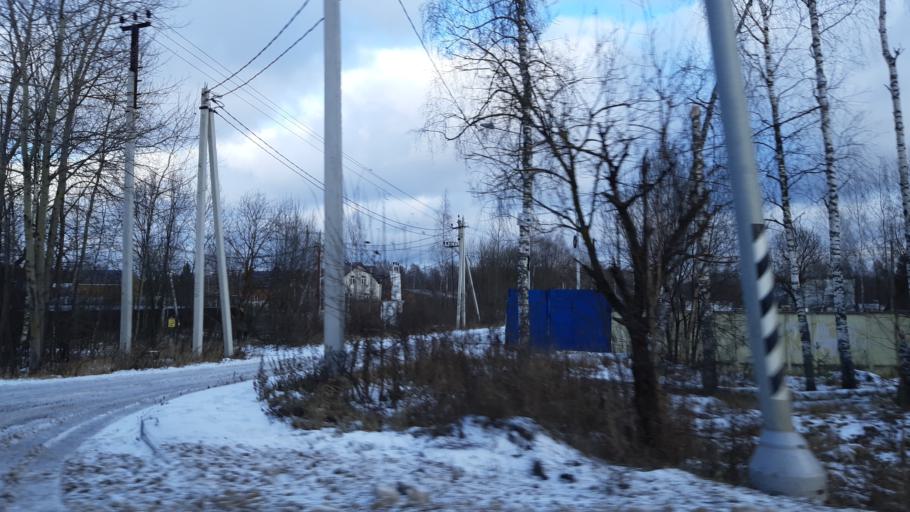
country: RU
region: Moskovskaya
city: Noginsk-9
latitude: 55.9532
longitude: 38.5500
